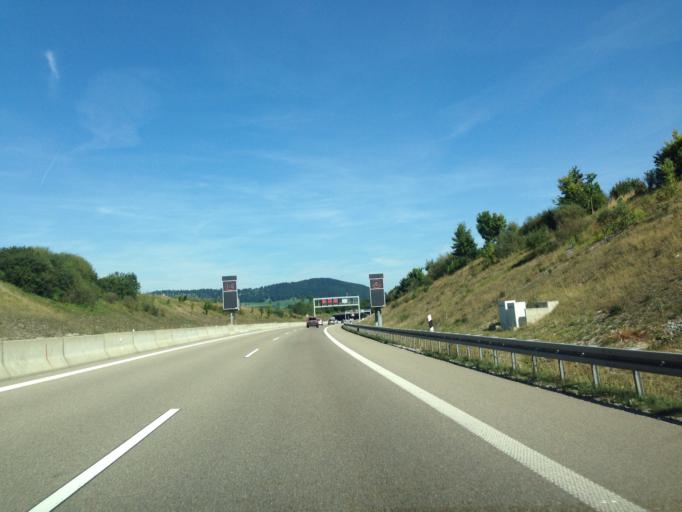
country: DE
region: Bavaria
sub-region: Swabia
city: Hopferau
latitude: 47.5946
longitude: 10.6562
